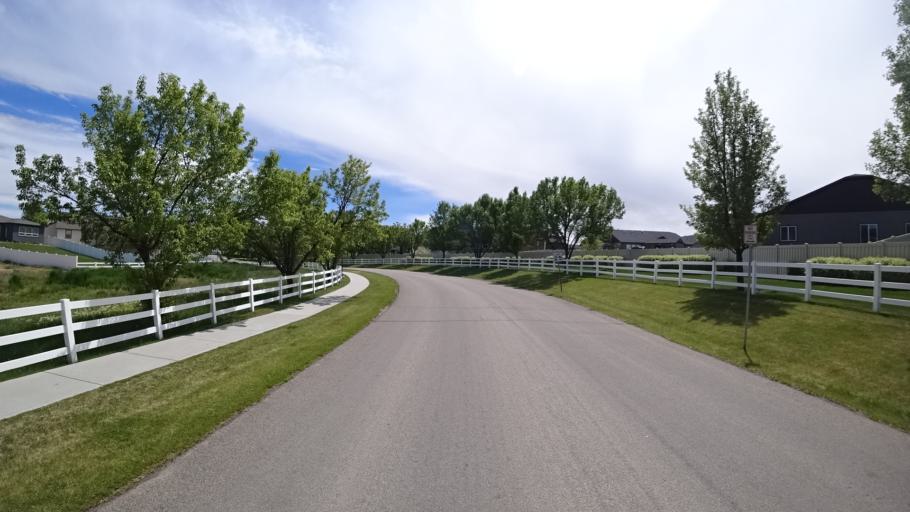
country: US
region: Idaho
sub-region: Ada County
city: Meridian
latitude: 43.5752
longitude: -116.4058
